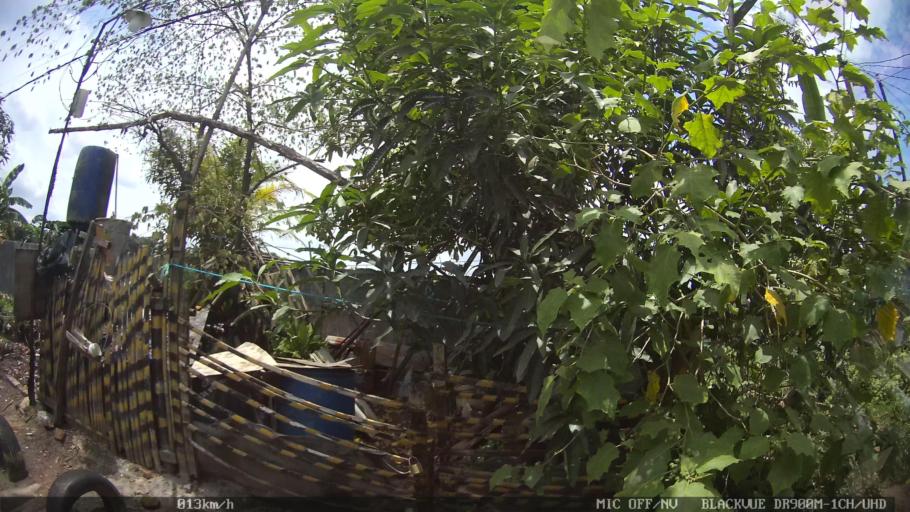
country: ID
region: North Sumatra
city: Medan
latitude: 3.6109
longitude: 98.7215
